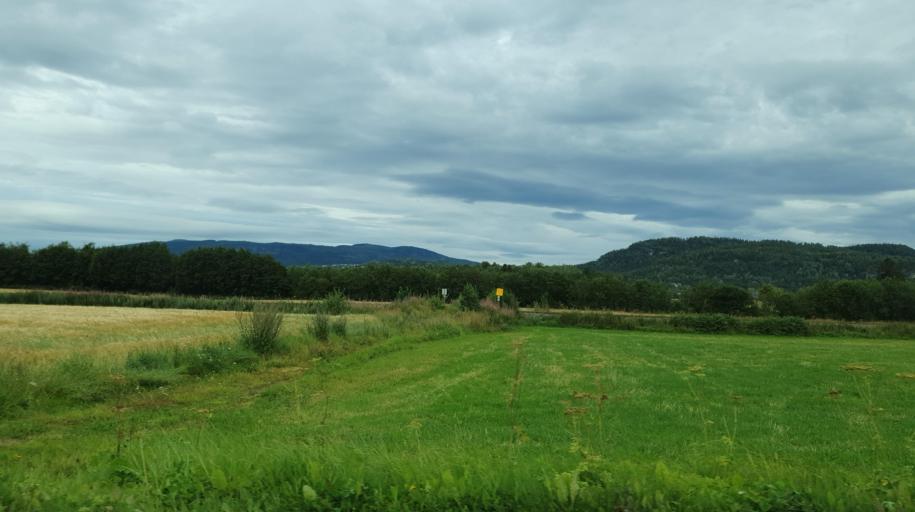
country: NO
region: Nord-Trondelag
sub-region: Stjordal
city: Stjordalshalsen
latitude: 63.4453
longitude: 10.9788
